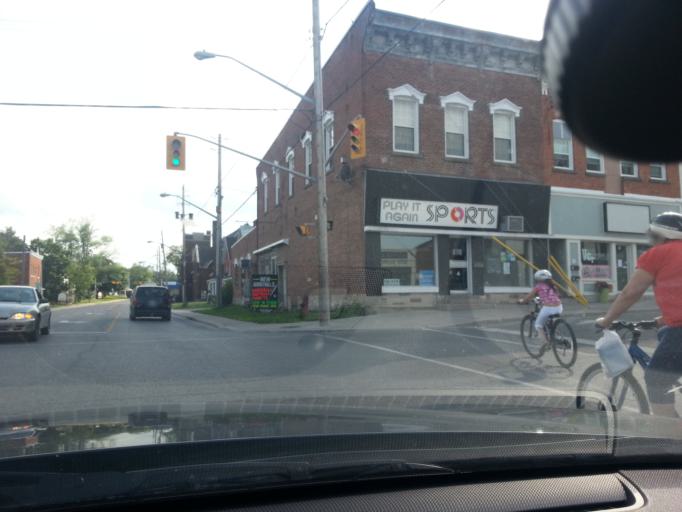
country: CA
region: Ontario
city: Arnprior
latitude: 45.4329
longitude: -76.3533
